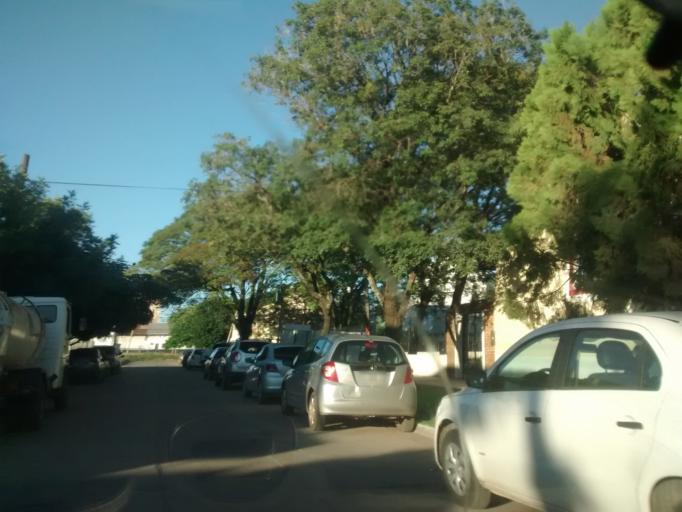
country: AR
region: Chaco
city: Resistencia
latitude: -27.4633
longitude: -58.9788
